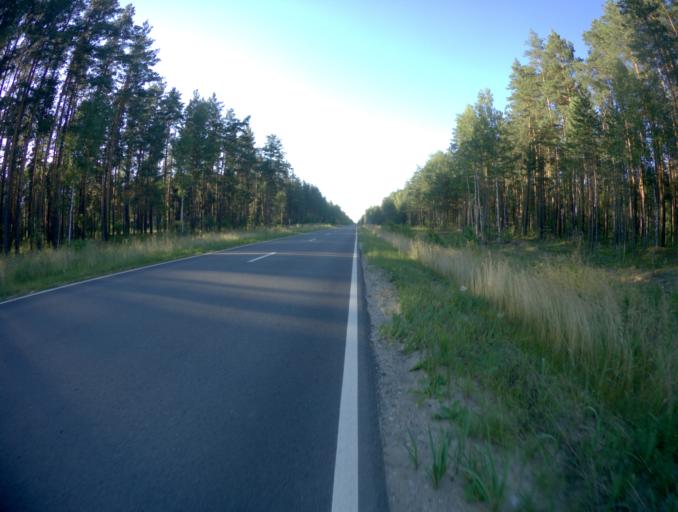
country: RU
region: Vladimir
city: Galitsy
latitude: 56.0666
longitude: 42.8665
